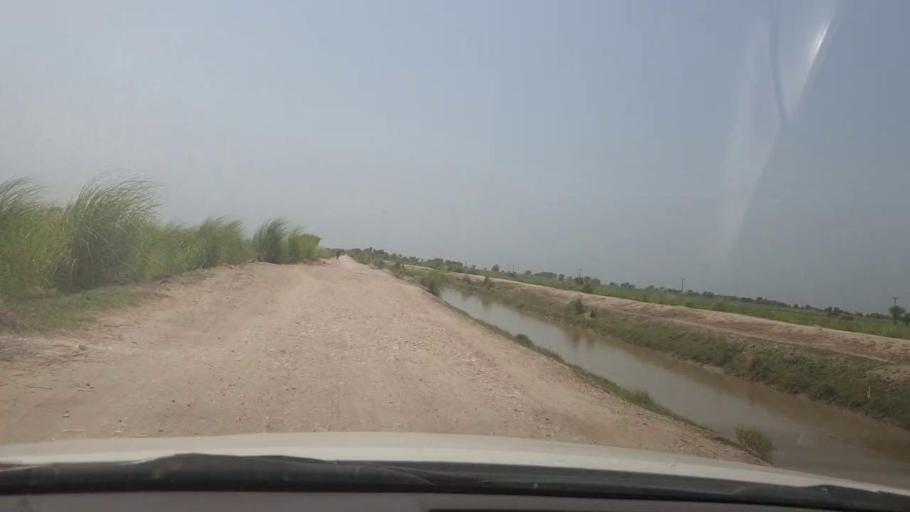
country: PK
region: Sindh
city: Shikarpur
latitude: 28.0516
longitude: 68.6005
